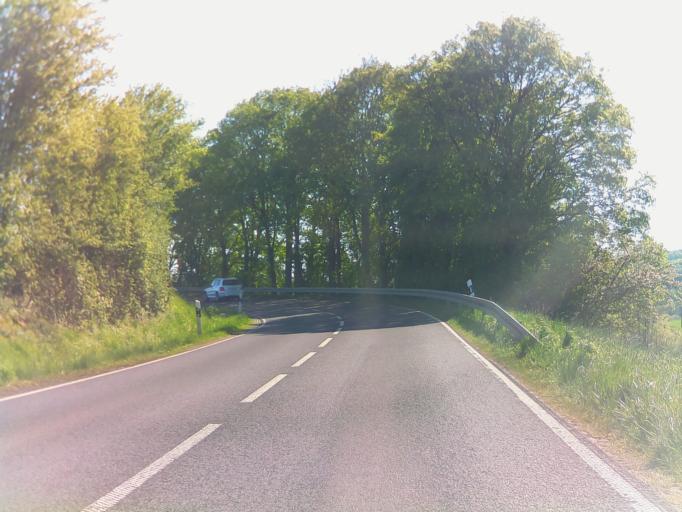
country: DE
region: Hesse
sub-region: Regierungsbezirk Darmstadt
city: Birstein
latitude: 50.3785
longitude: 9.2998
